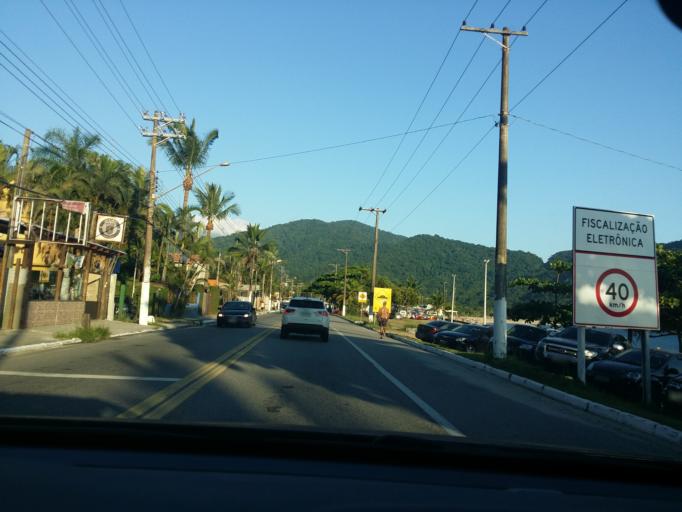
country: BR
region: Sao Paulo
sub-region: Sao Sebastiao
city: Sao Sebastiao
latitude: -23.7830
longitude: -45.6333
